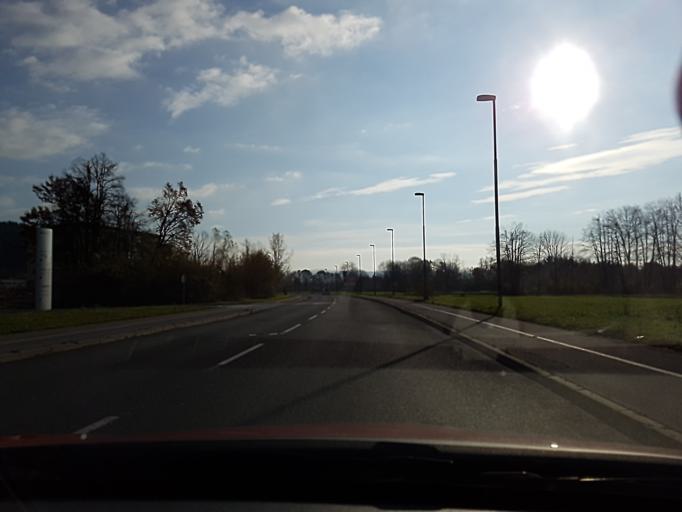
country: SI
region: Trzin
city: Trzin
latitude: 46.0944
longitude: 14.5508
